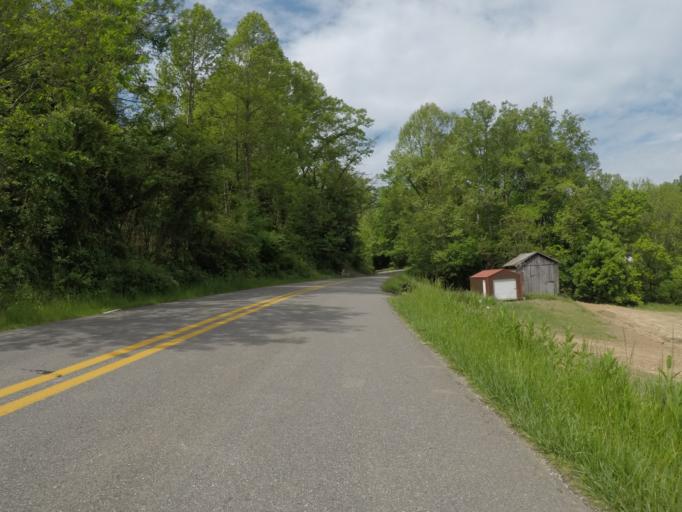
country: US
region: West Virginia
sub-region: Wayne County
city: Ceredo
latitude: 38.3416
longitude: -82.5724
